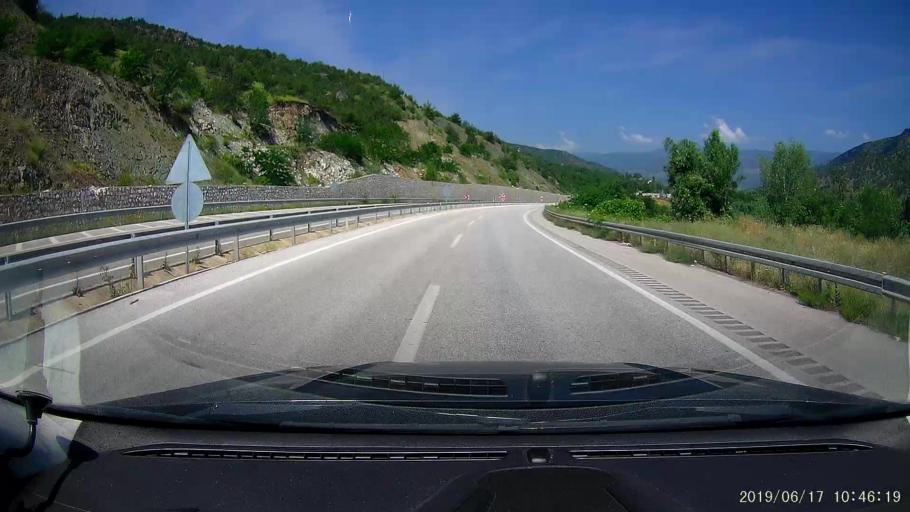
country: TR
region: Corum
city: Hacihamza
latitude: 41.0664
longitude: 34.4648
